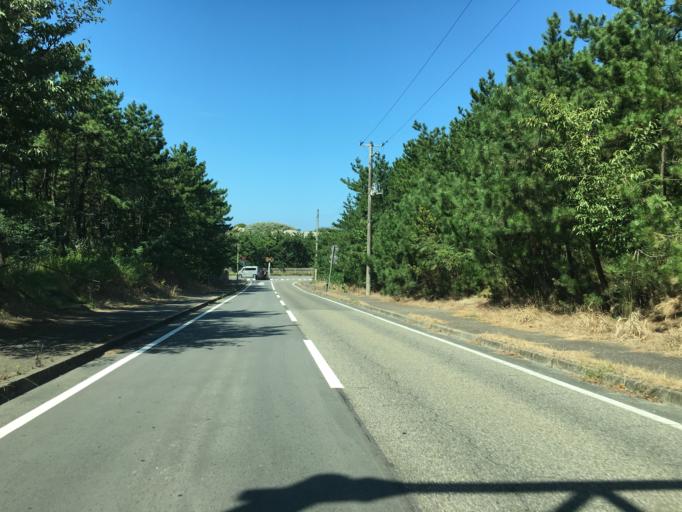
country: JP
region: Niigata
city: Niigata-shi
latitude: 37.9012
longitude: 138.9921
